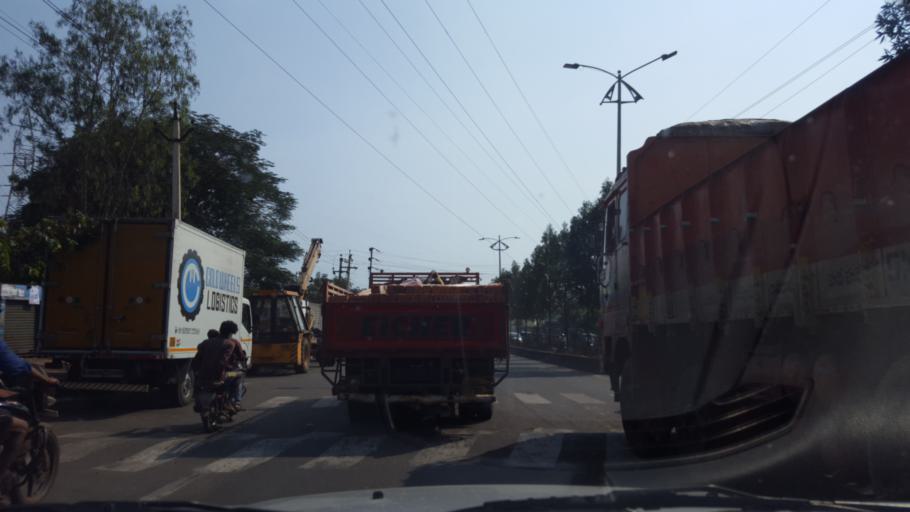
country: IN
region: Andhra Pradesh
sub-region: Vishakhapatnam
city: Visakhapatnam
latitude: 17.6822
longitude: 83.1938
